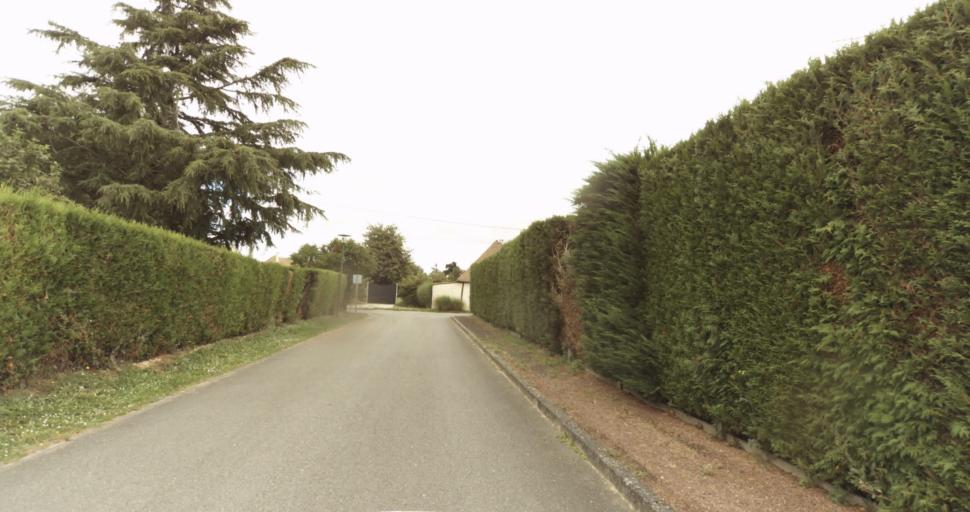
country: FR
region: Haute-Normandie
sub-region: Departement de l'Eure
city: Marcilly-sur-Eure
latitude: 48.9212
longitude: 1.2497
